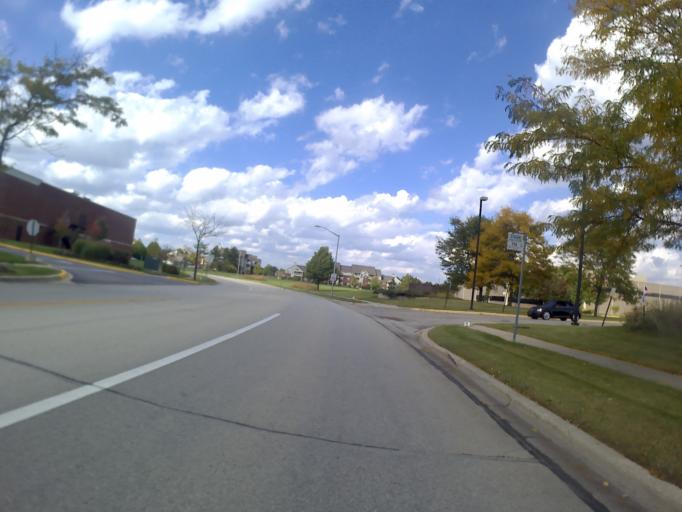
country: US
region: Illinois
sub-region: DuPage County
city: Wheaton
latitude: 41.8314
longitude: -88.0959
